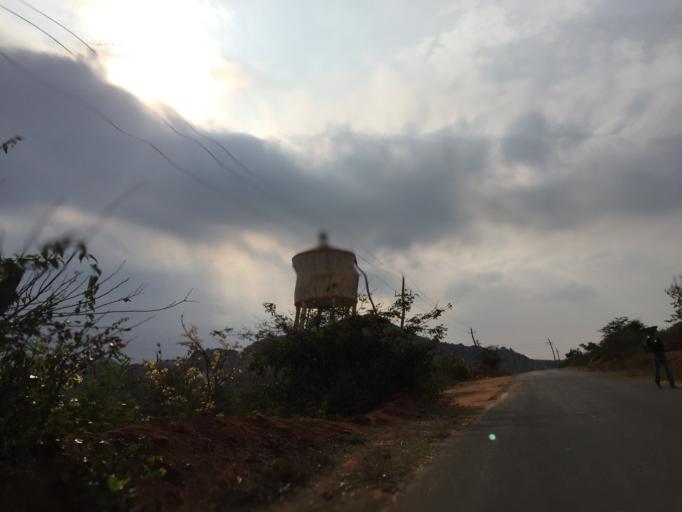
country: IN
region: Karnataka
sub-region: Chikkaballapur
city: Chik Ballapur
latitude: 13.5522
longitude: 77.7494
